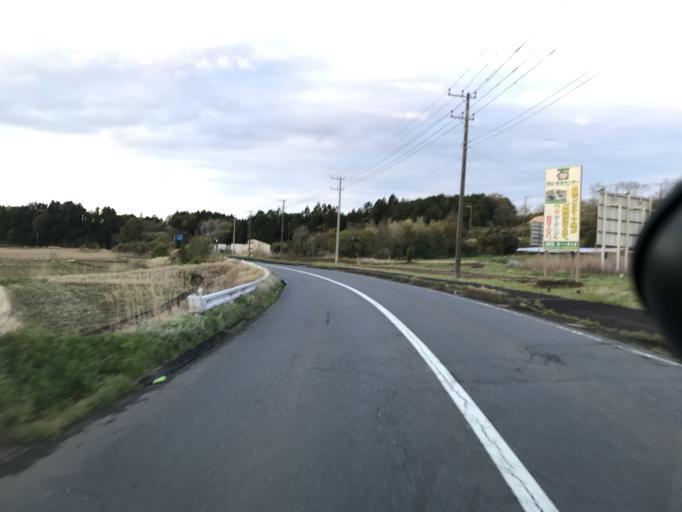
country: JP
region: Chiba
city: Sawara
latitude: 35.8142
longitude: 140.4936
